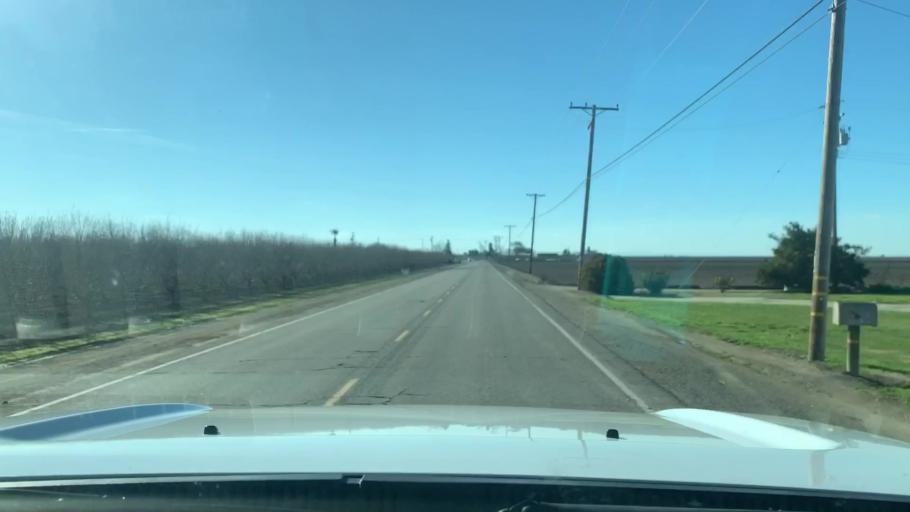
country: US
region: California
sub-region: Tulare County
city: Tulare
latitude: 36.1812
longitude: -119.4532
